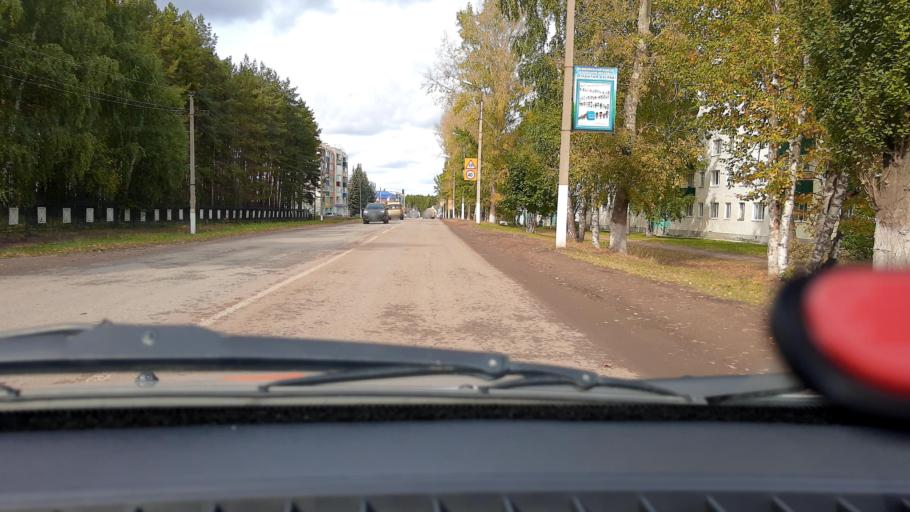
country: RU
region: Bashkortostan
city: Belebey
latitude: 54.1031
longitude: 54.0965
